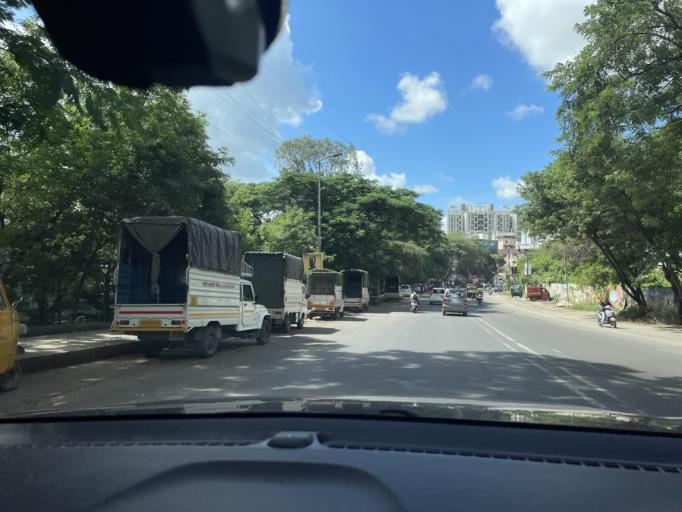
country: IN
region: Maharashtra
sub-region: Pune Division
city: Shivaji Nagar
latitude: 18.5181
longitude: 73.7798
